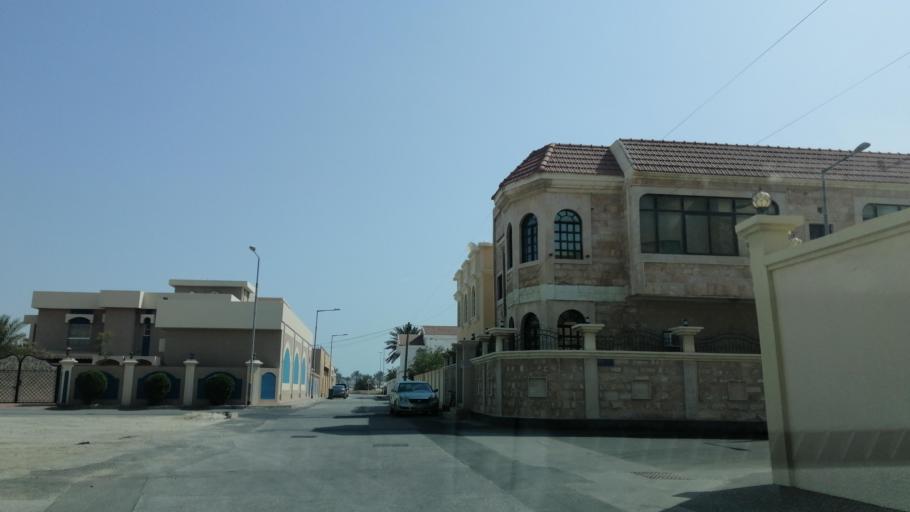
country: BH
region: Muharraq
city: Al Hadd
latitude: 26.2496
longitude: 50.6559
